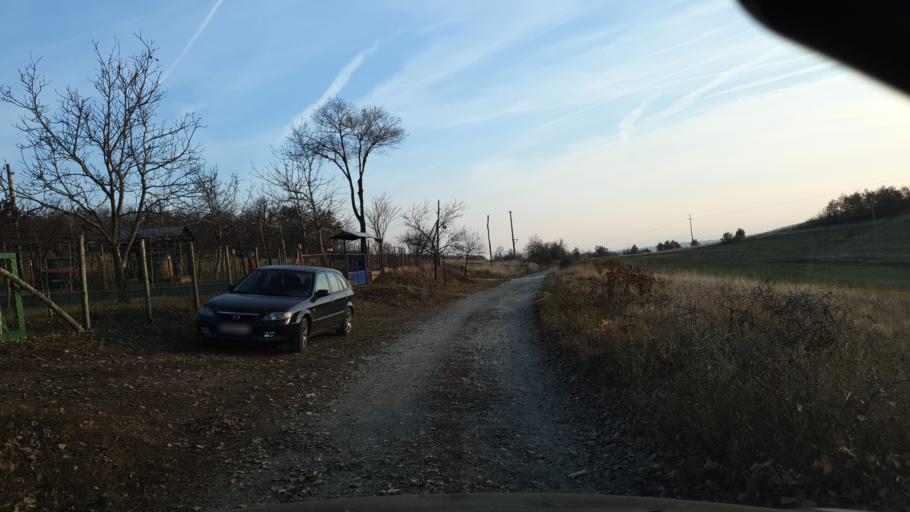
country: RS
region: Central Serbia
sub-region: Borski Okrug
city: Bor
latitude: 44.0657
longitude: 22.0795
